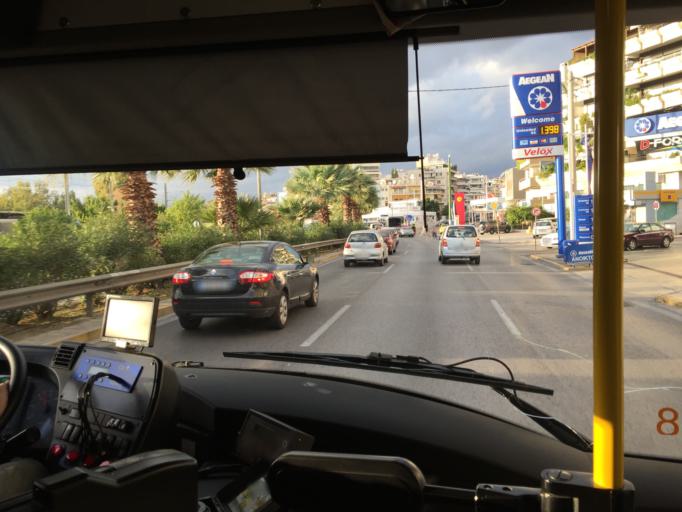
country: GR
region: Attica
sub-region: Nomarchia Athinas
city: Alimos
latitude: 37.9130
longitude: 23.7092
